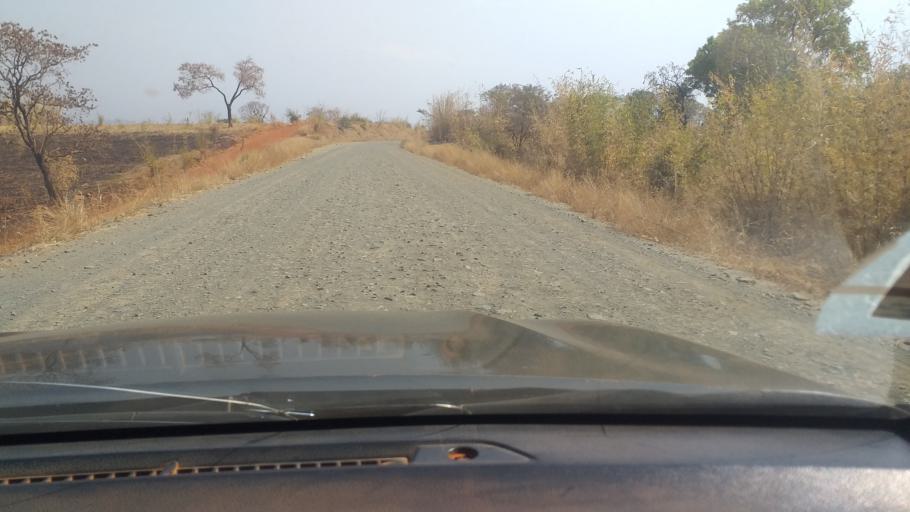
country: ET
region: Binshangul Gumuz
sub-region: Asosa
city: Asosa
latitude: 10.0506
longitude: 34.7934
